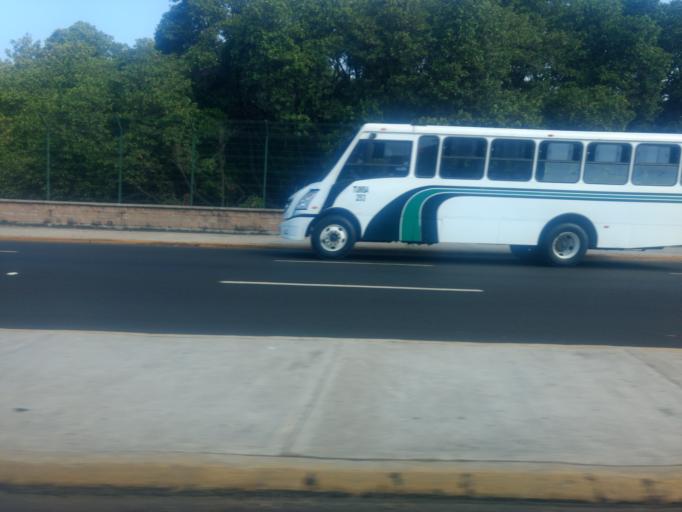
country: MX
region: Colima
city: Tapeixtles
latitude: 19.0671
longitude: -104.2870
